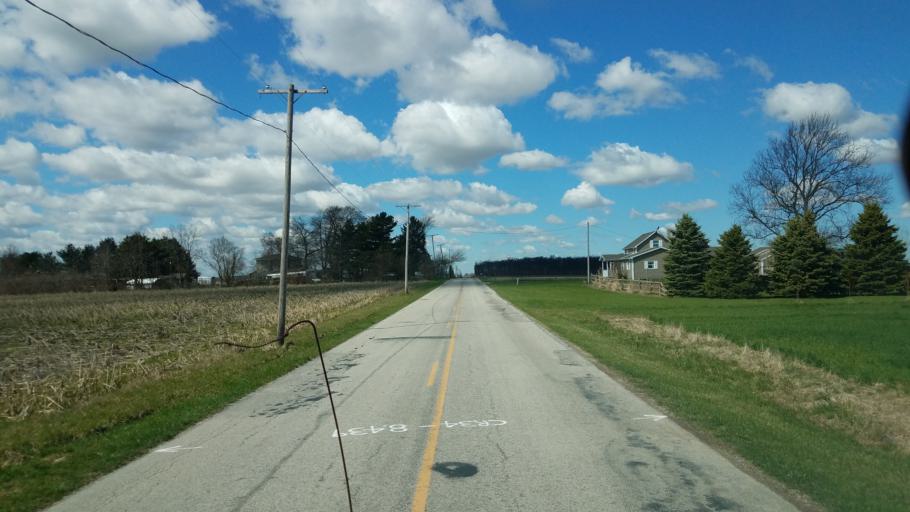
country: US
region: Ohio
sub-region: Sandusky County
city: Mount Carmel
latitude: 41.2417
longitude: -82.9682
